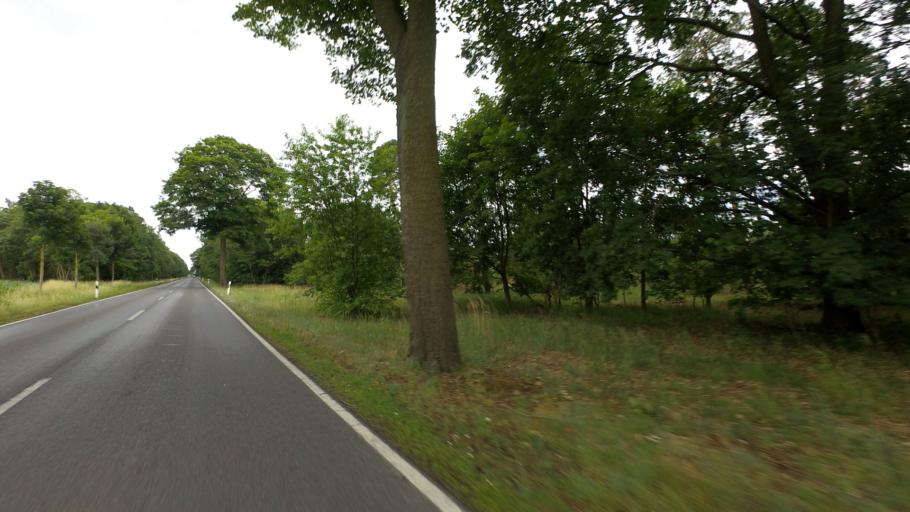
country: DE
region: Brandenburg
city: Crinitz
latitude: 51.8049
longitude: 13.8267
